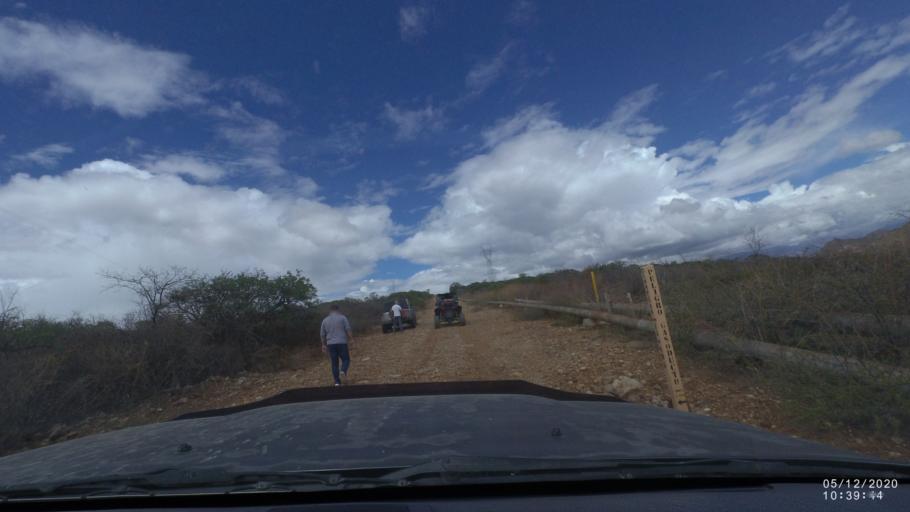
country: BO
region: Cochabamba
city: Sipe Sipe
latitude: -17.5457
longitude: -66.2848
